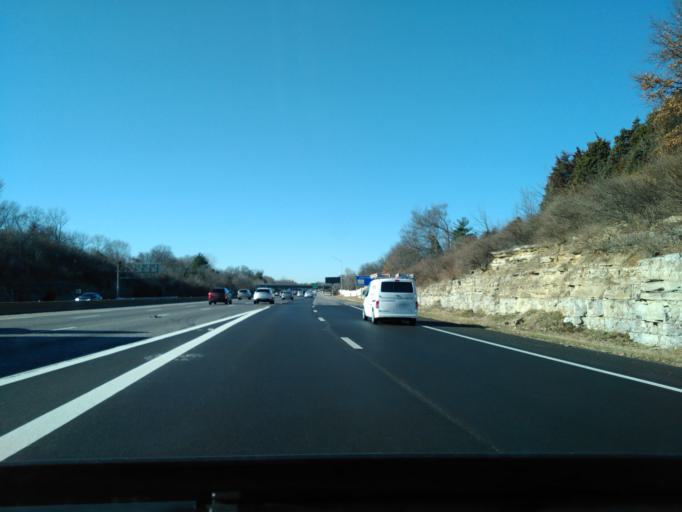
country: US
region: Missouri
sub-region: Saint Louis County
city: Concord
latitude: 38.5141
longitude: -90.3741
